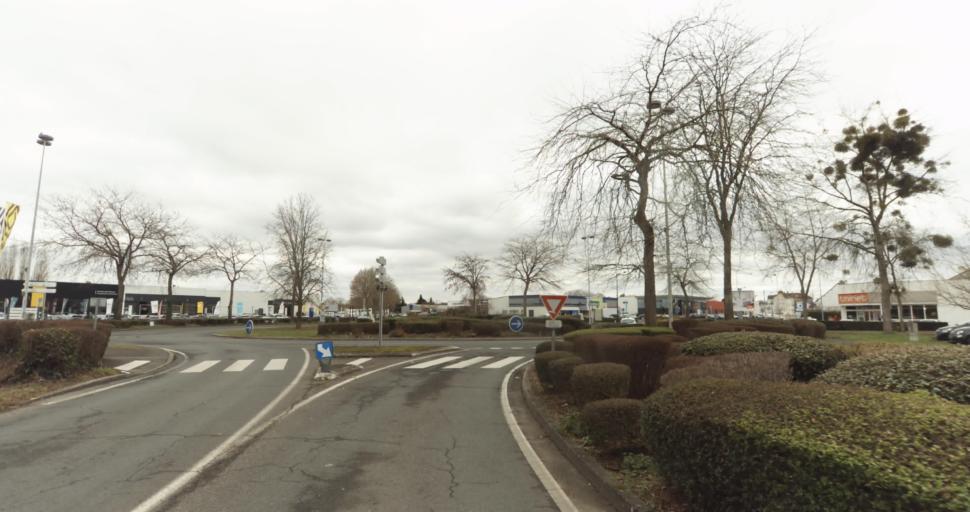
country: FR
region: Pays de la Loire
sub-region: Departement de Maine-et-Loire
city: Saumur
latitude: 47.2752
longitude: -0.0612
